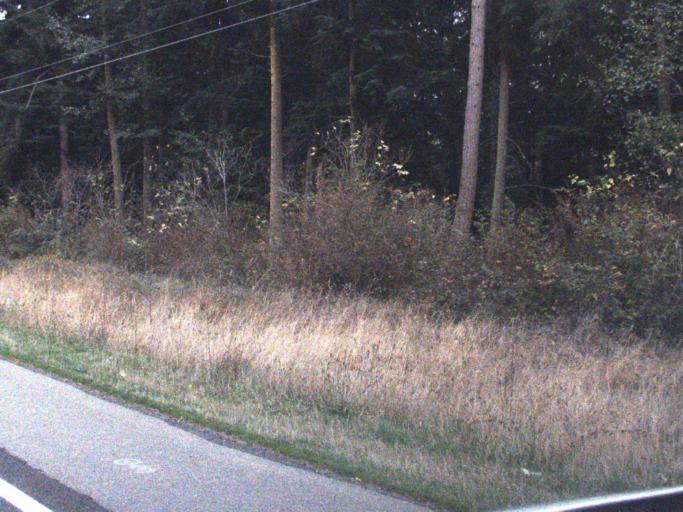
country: US
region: Washington
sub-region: Island County
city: Camano
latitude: 48.1321
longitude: -122.5903
